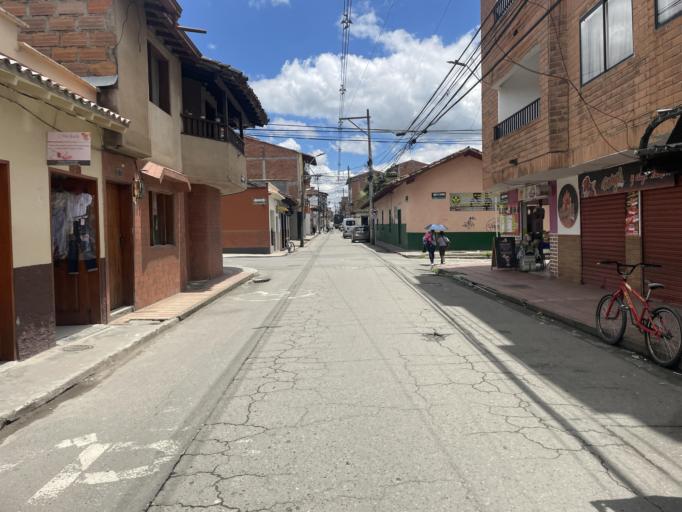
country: CO
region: Antioquia
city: La Ceja
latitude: 6.0278
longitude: -75.4321
